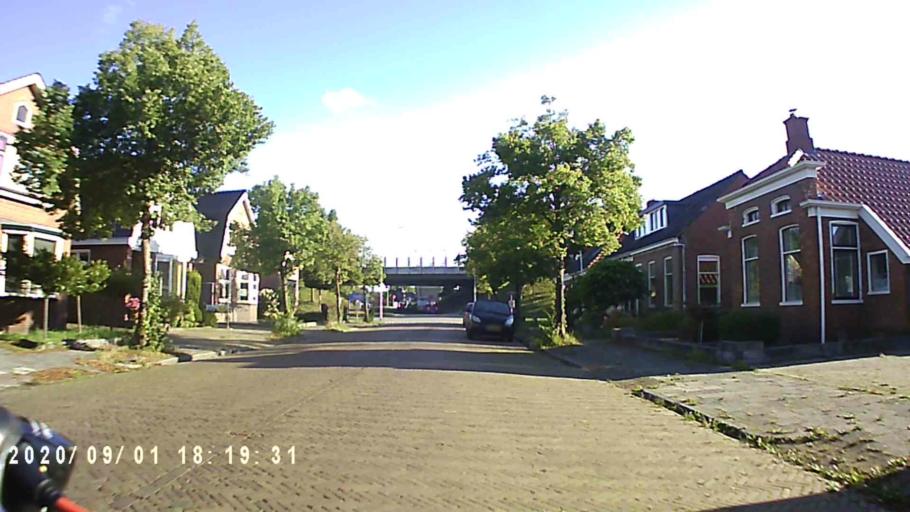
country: NL
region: Groningen
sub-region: Gemeente Hoogezand-Sappemeer
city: Sappemeer
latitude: 53.1695
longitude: 6.7891
